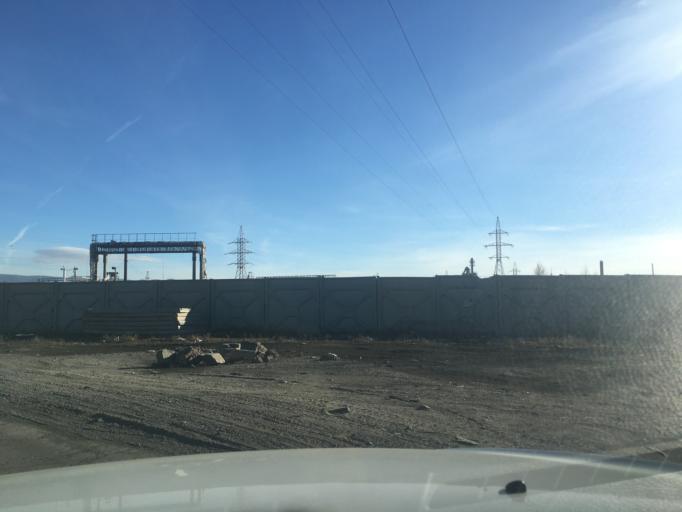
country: MN
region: Ulaanbaatar
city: Ulaanbaatar
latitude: 47.9010
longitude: 106.7347
